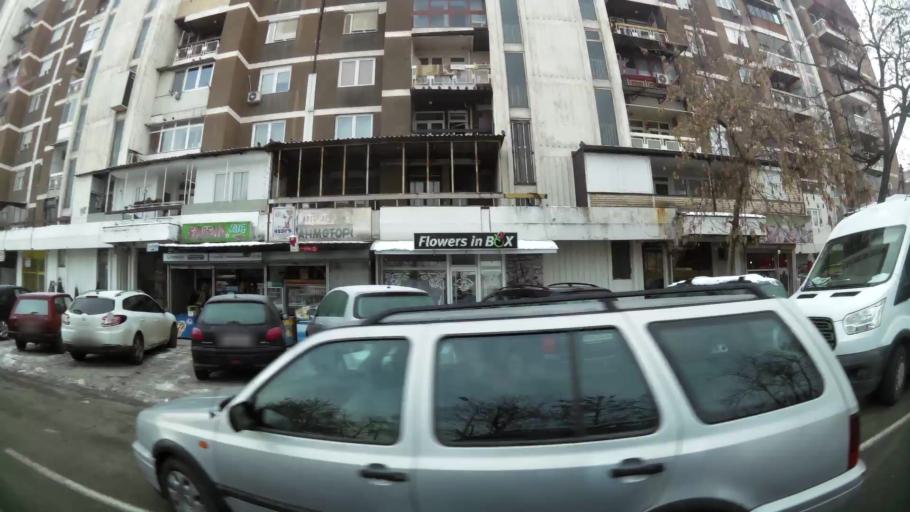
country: MK
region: Cair
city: Cair
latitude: 42.0129
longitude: 21.4333
